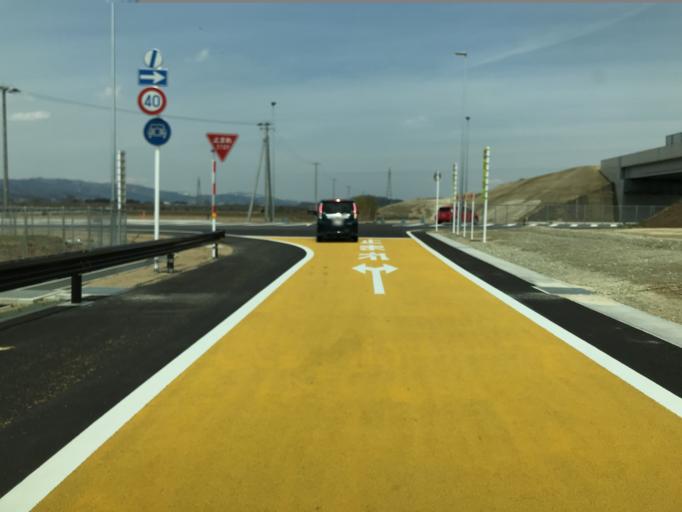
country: JP
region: Yamagata
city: Higashine
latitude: 38.4466
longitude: 140.3534
